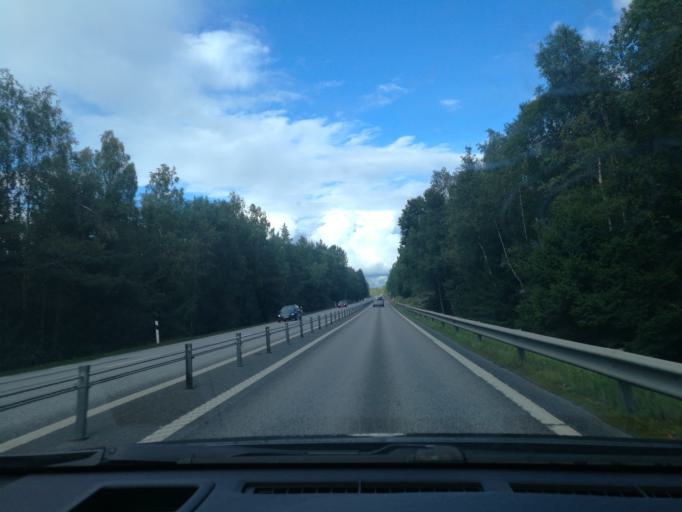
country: SE
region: OEstergoetland
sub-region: Norrkopings Kommun
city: Jursla
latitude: 58.7170
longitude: 16.1654
